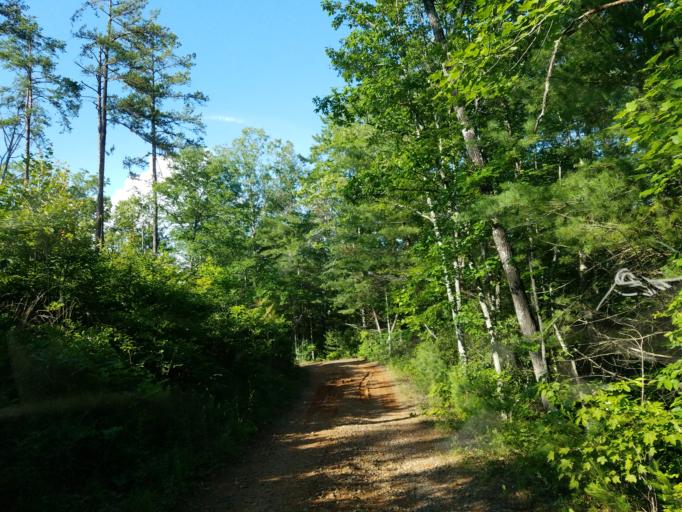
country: US
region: Georgia
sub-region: Fannin County
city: Blue Ridge
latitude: 34.7939
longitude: -84.1968
